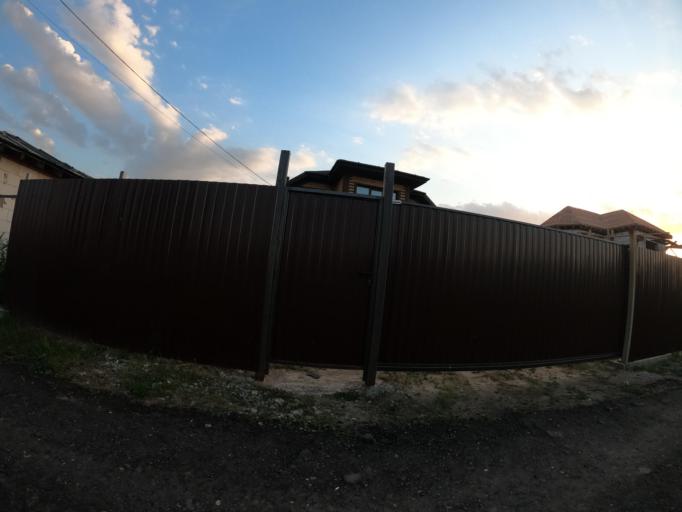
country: RU
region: Moskovskaya
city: Ramenskoye
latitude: 55.5597
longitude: 38.3052
